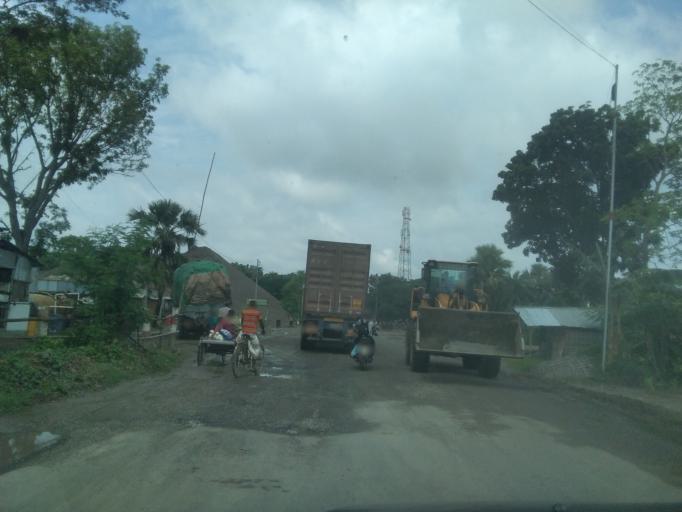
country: BD
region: Khulna
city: Kesabpur
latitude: 22.8162
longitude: 89.2519
